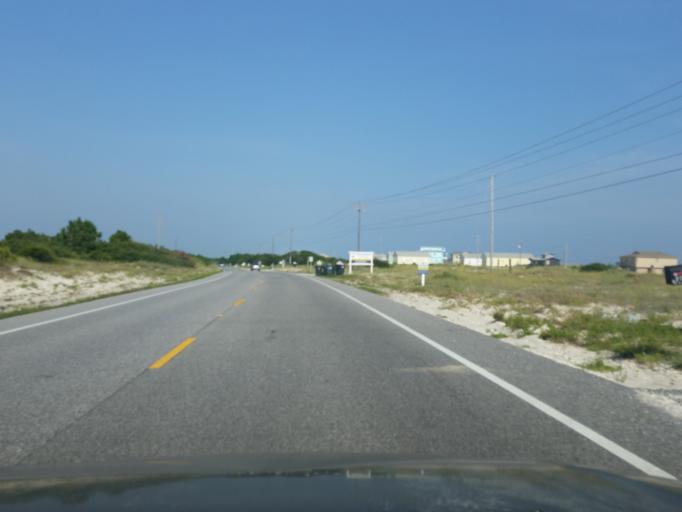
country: US
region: Alabama
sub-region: Mobile County
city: Dauphin Island
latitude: 30.2334
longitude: -87.9429
